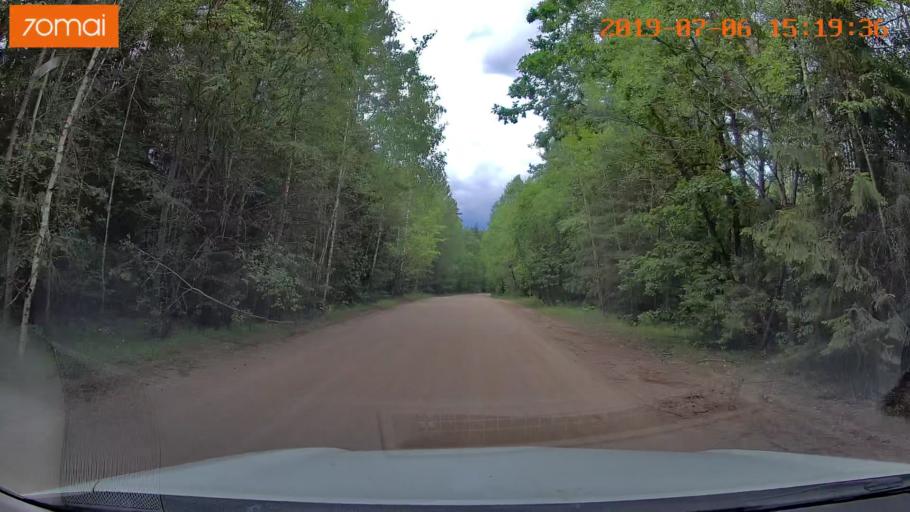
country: BY
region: Minsk
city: Valozhyn
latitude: 53.9990
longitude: 26.6451
